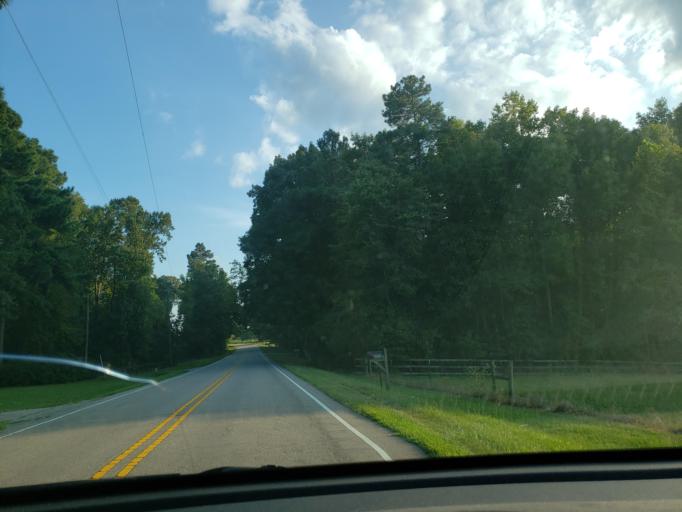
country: US
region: North Carolina
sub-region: Vance County
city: Henderson
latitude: 36.3871
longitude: -78.3682
